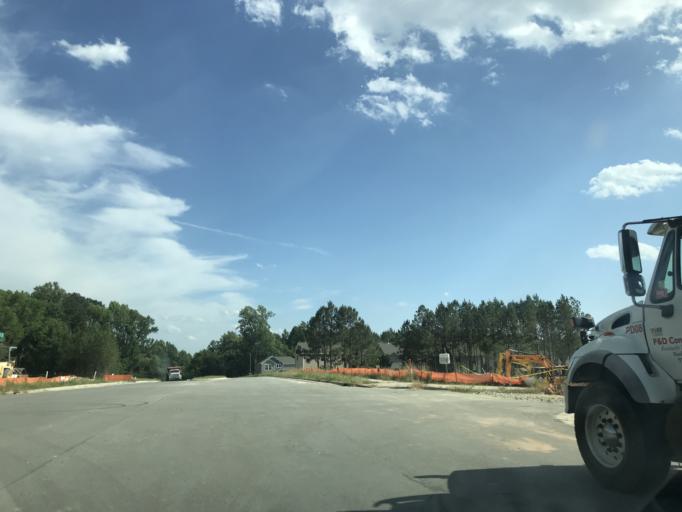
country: US
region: North Carolina
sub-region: Wake County
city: Garner
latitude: 35.7225
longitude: -78.5603
